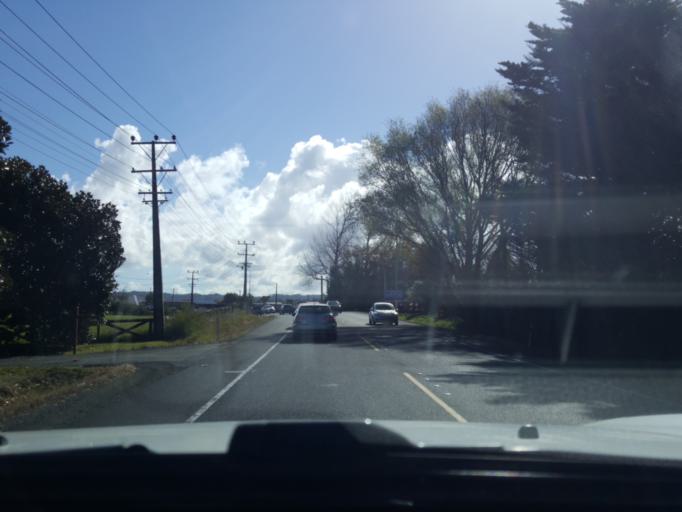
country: NZ
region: Auckland
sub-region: Auckland
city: Muriwai Beach
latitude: -36.7819
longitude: 174.5705
